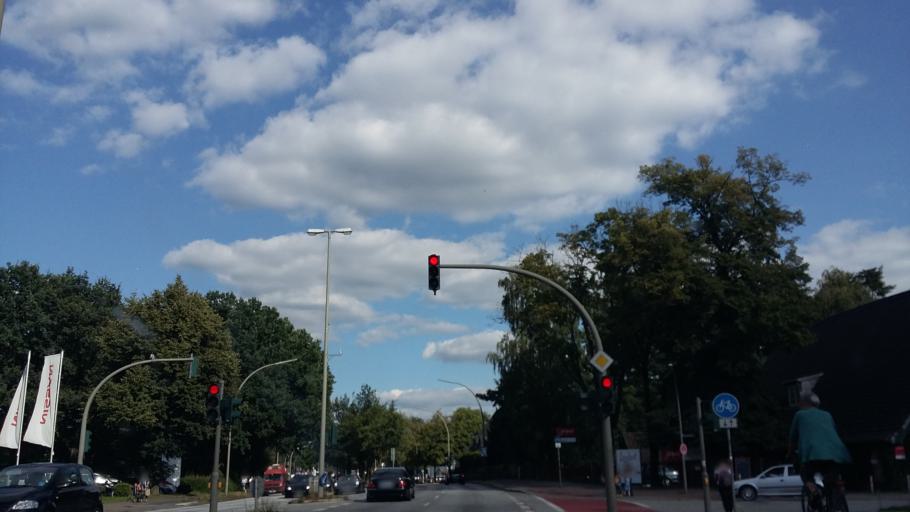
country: DE
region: Schleswig-Holstein
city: Halstenbek
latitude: 53.5730
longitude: 9.8426
